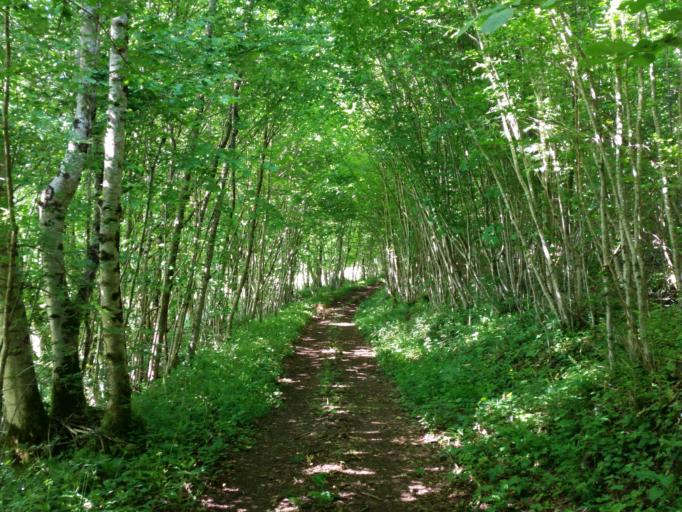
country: FR
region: Franche-Comte
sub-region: Departement du Doubs
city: Quingey
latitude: 47.0353
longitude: 5.9682
